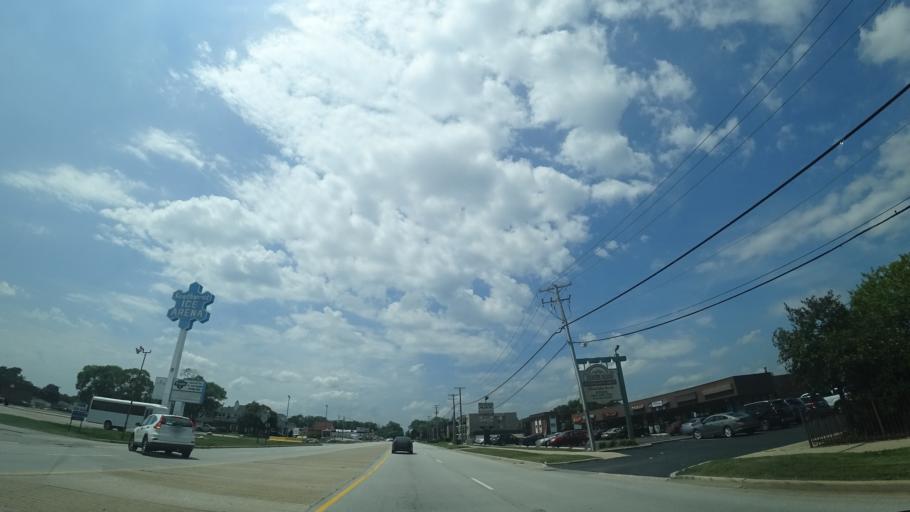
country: US
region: Illinois
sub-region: Cook County
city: Crestwood
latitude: 41.6615
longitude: -87.7544
